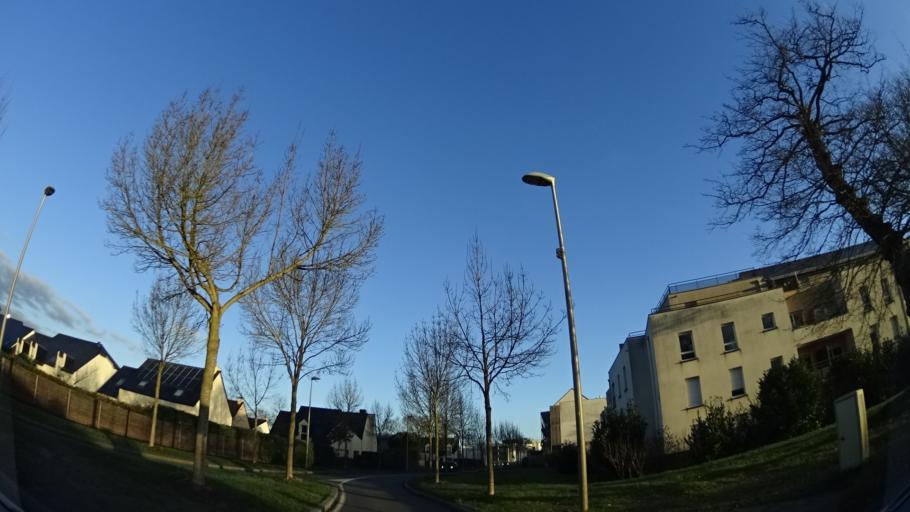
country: FR
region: Brittany
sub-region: Departement d'Ille-et-Vilaine
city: Betton
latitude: 48.1770
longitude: -1.6618
